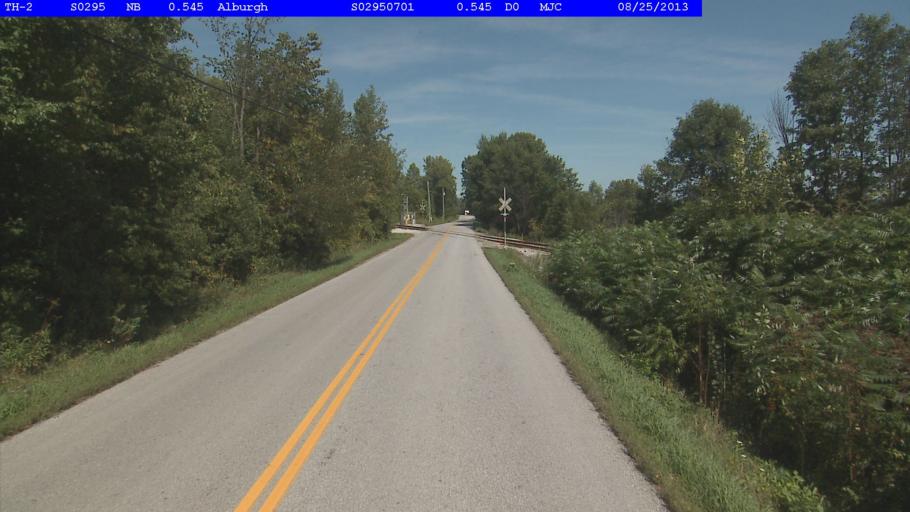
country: US
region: Vermont
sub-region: Franklin County
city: Swanton
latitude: 44.9821
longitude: -73.2283
